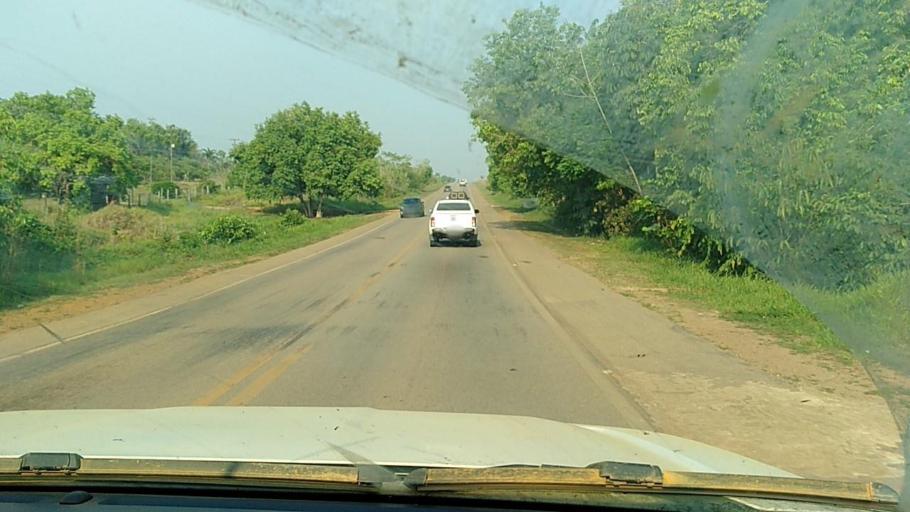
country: BR
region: Rondonia
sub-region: Porto Velho
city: Porto Velho
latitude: -8.7406
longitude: -63.9372
